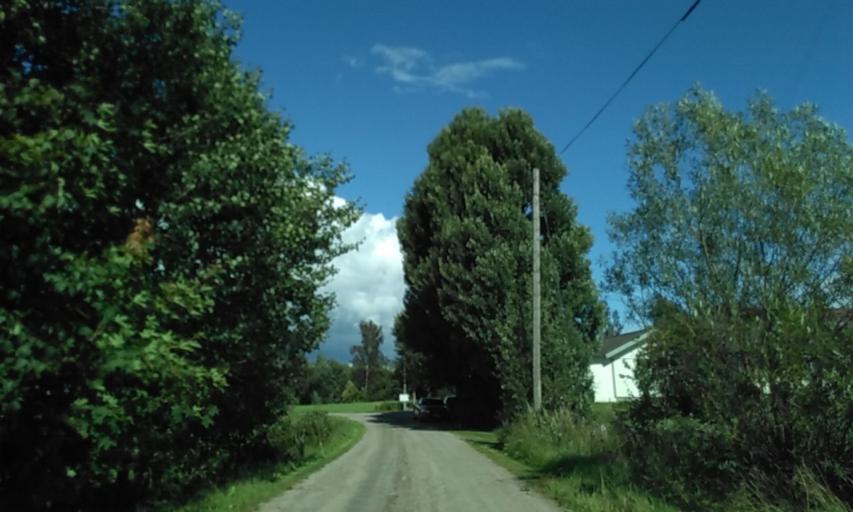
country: SE
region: Vaestra Goetaland
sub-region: Vargarda Kommun
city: Jonstorp
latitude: 57.9970
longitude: 12.7223
